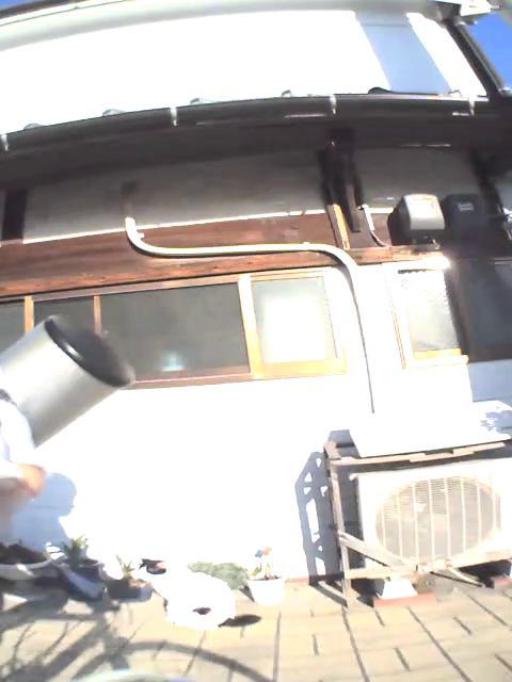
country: JP
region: Yamaguchi
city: Nagato
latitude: 34.3952
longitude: 131.1984
